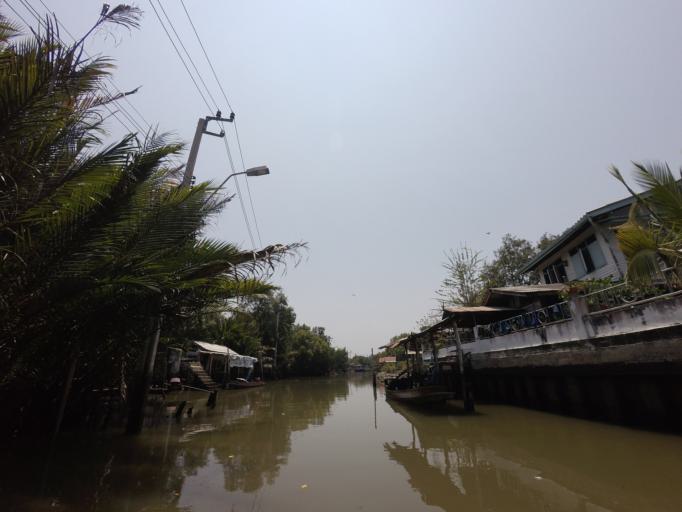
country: TH
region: Bangkok
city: Thung Khru
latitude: 13.5448
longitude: 100.4996
